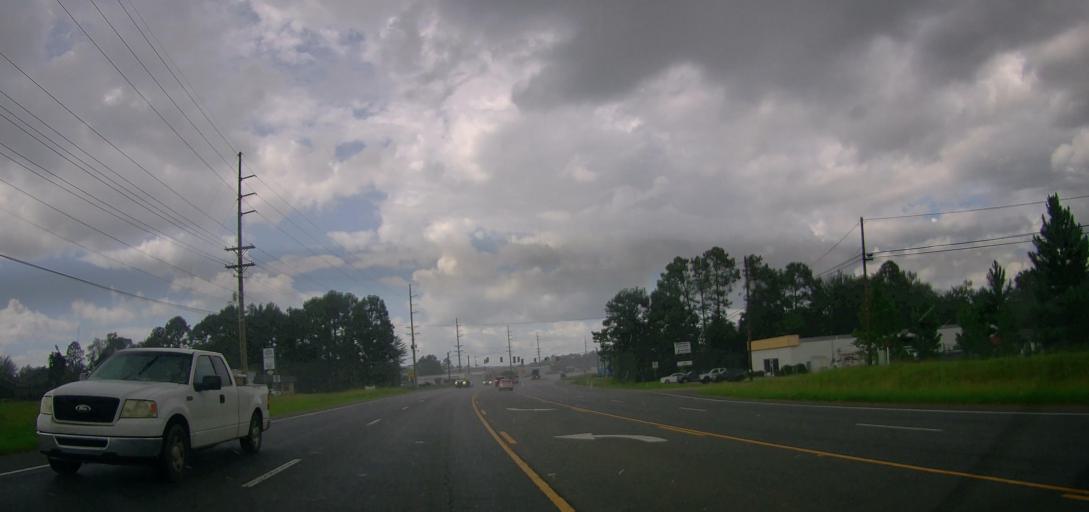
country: US
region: Georgia
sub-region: Coffee County
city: Douglas
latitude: 31.5006
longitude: -82.8745
